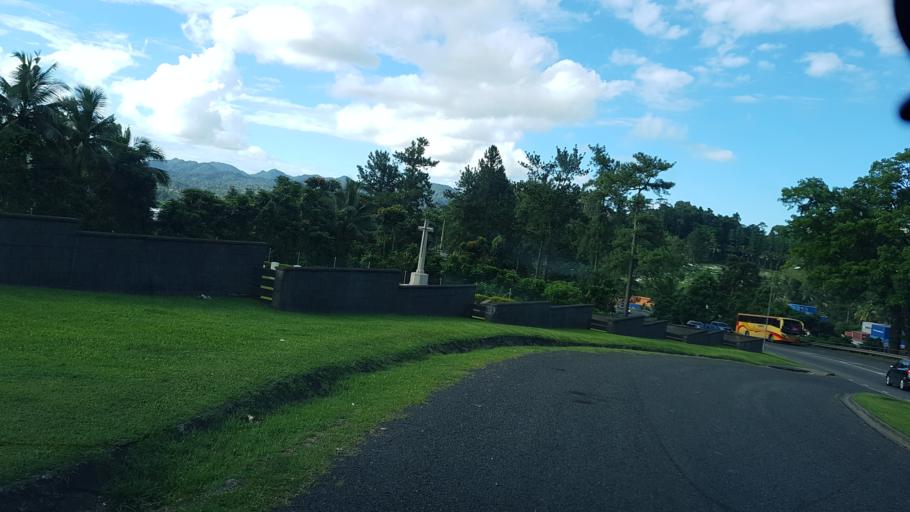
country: FJ
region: Central
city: Suva
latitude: -18.1226
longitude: 178.4340
